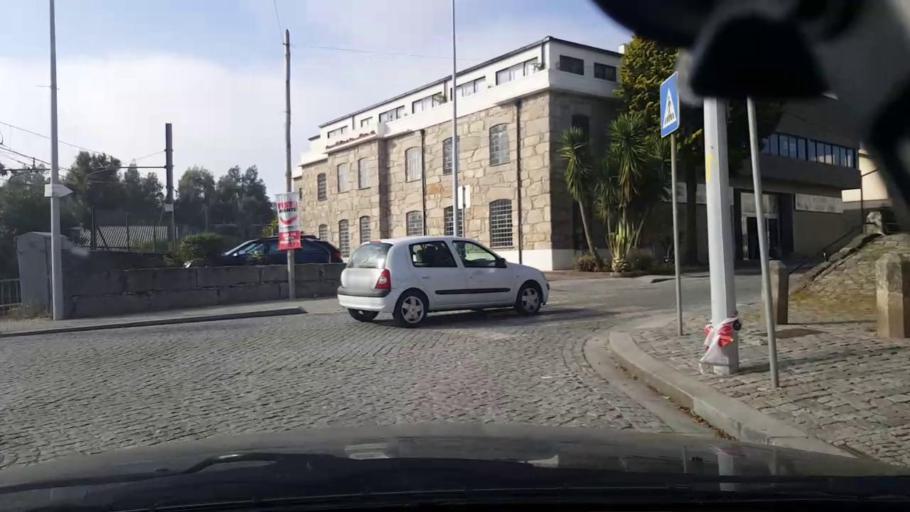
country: PT
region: Porto
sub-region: Maia
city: Gemunde
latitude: 41.2708
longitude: -8.6798
